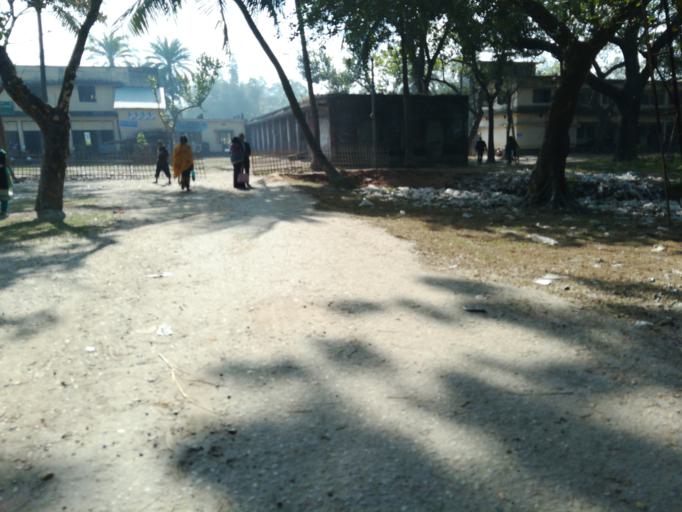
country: BD
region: Rangpur Division
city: Rangpur
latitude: 25.5687
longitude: 89.2734
